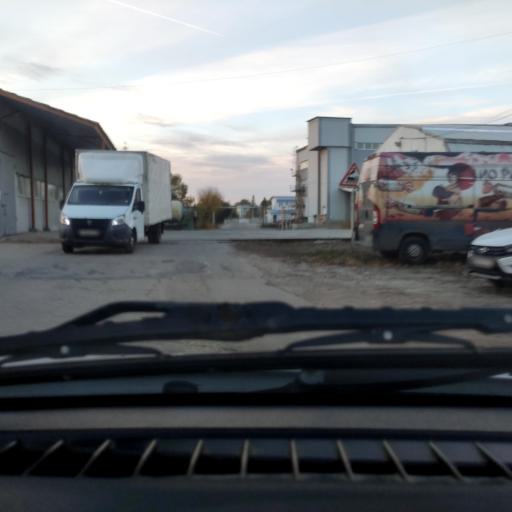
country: RU
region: Samara
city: Zhigulevsk
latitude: 53.4833
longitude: 49.4922
